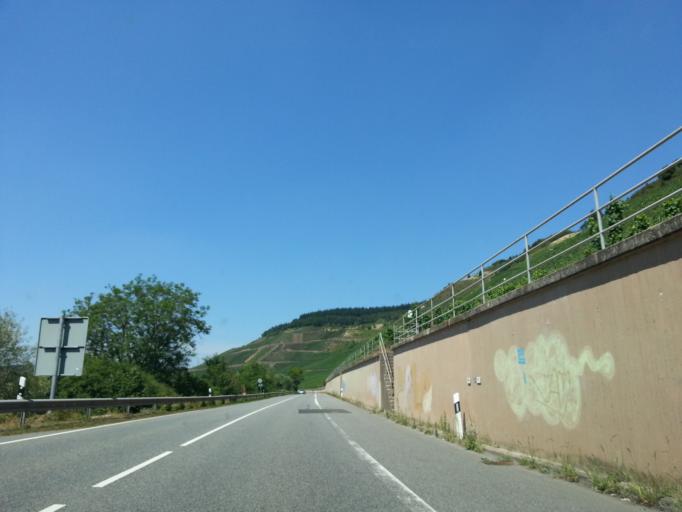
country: DE
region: Rheinland-Pfalz
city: Longuich
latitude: 49.8090
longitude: 6.7770
